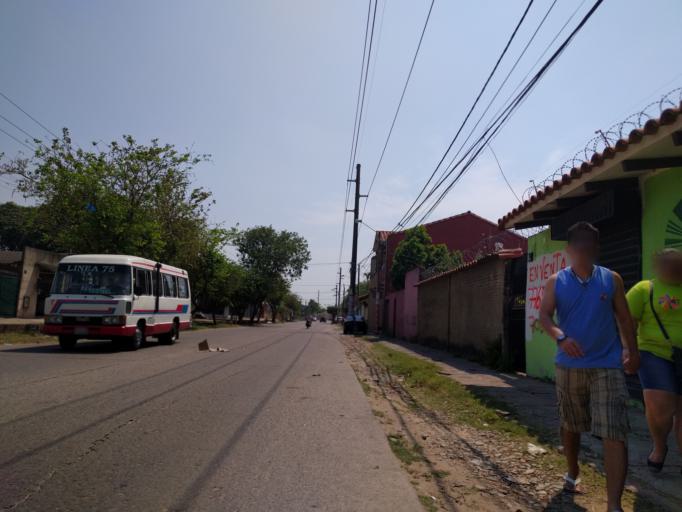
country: BO
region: Santa Cruz
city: Santa Cruz de la Sierra
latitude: -17.7949
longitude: -63.1568
